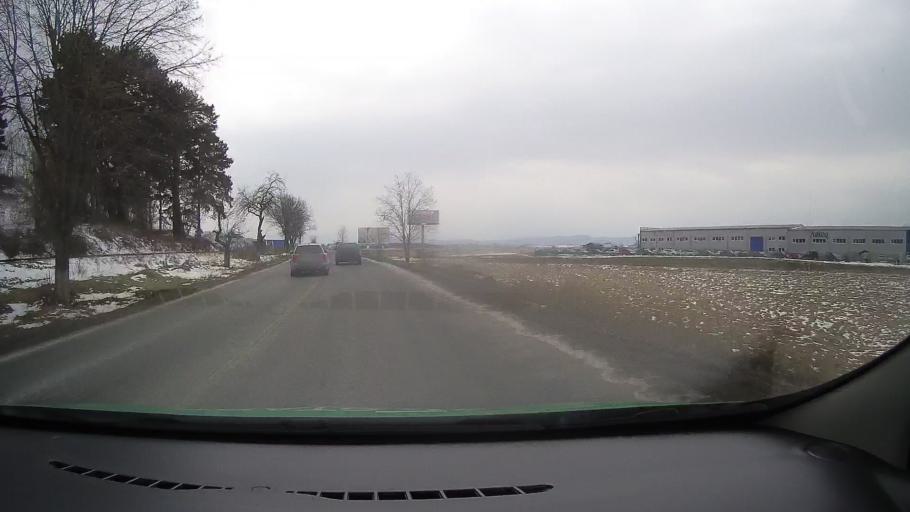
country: RO
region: Brasov
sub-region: Comuna Ghimbav
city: Ghimbav
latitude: 45.6417
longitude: 25.5093
